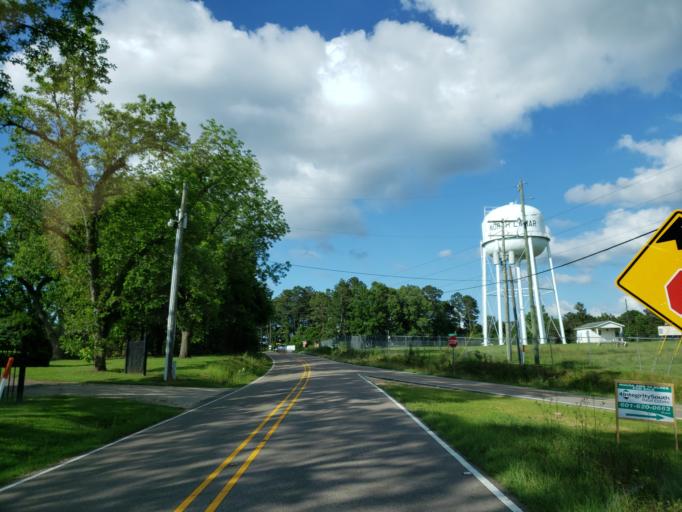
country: US
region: Mississippi
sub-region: Lamar County
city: West Hattiesburg
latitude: 31.2734
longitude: -89.3540
